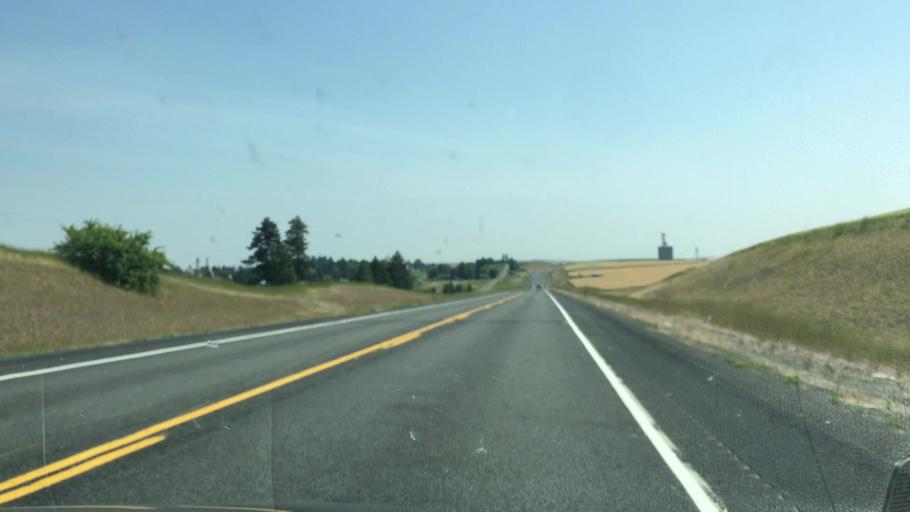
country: US
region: Idaho
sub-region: Lewis County
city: Nezperce
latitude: 46.2376
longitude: -116.4858
